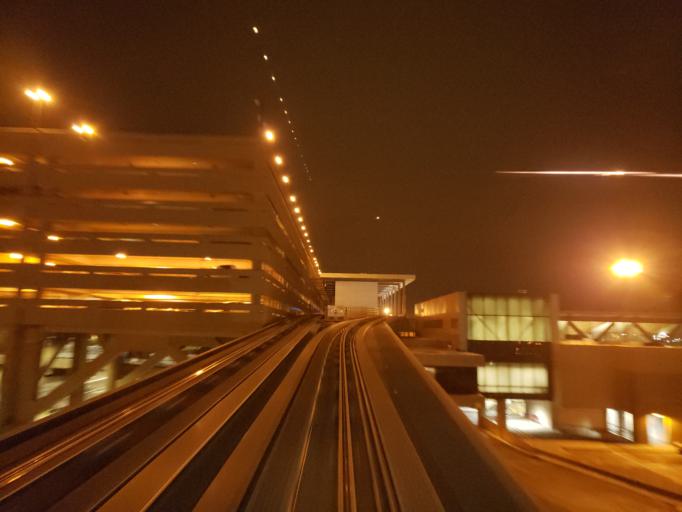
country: US
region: Arizona
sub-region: Maricopa County
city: Tempe Junction
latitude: 33.4348
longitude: -112.0002
